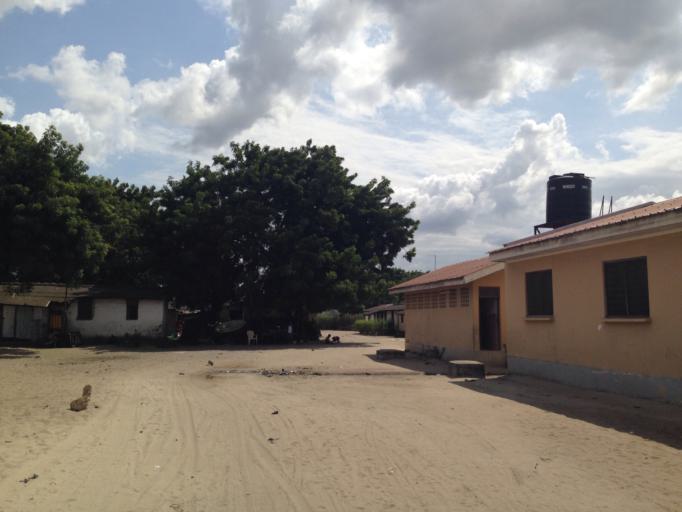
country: TZ
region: Dar es Salaam
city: Dar es Salaam
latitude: -6.8426
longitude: 39.2821
